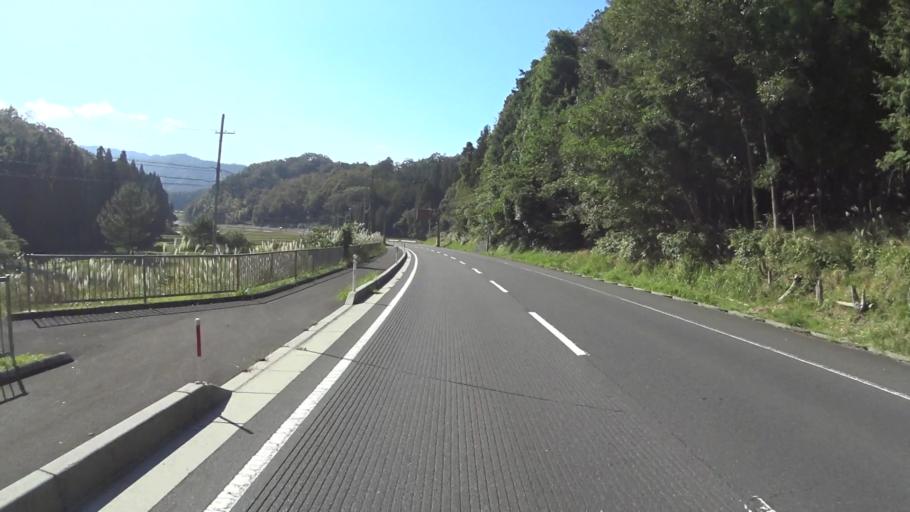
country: JP
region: Hyogo
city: Toyooka
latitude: 35.5763
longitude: 134.9903
